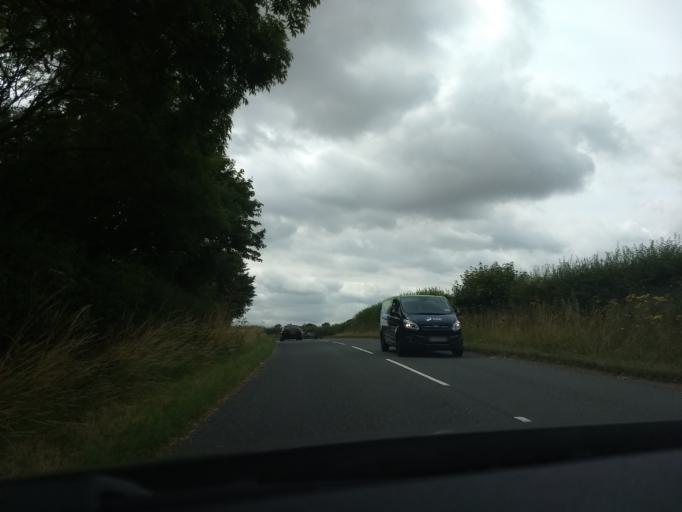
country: GB
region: England
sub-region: Suffolk
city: Ipswich
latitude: 52.0112
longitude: 1.1661
